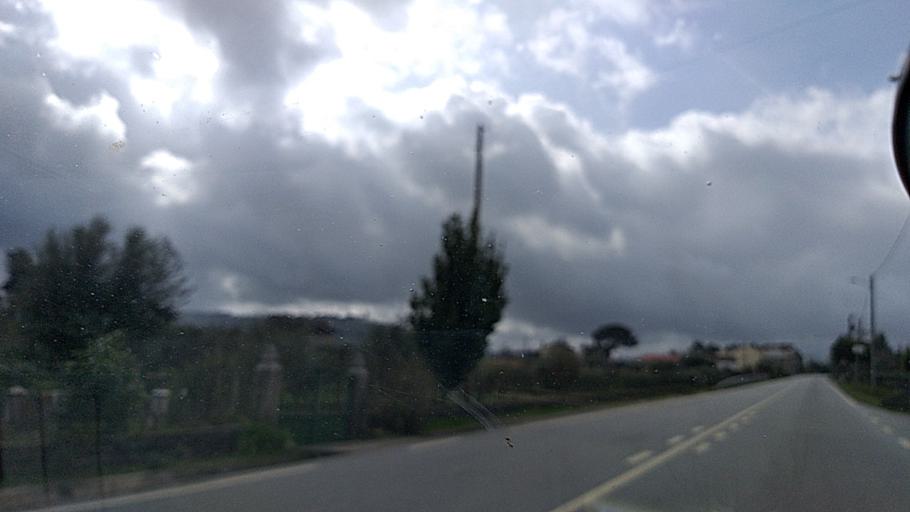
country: PT
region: Viseu
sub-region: Mangualde
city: Mangualde
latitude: 40.6310
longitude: -7.7479
